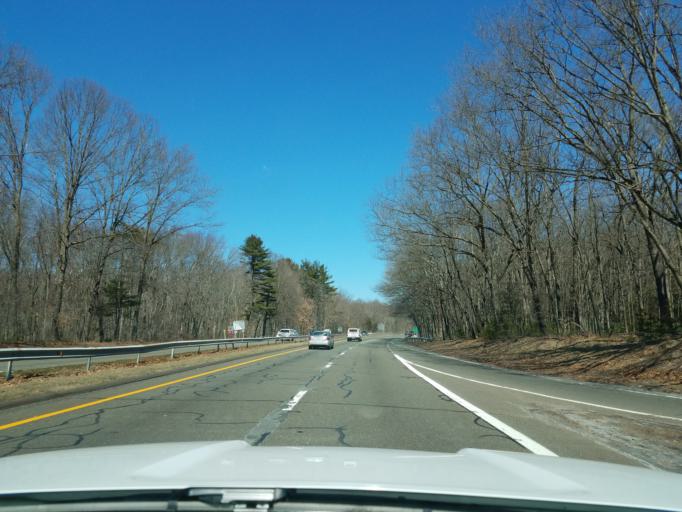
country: US
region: Connecticut
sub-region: New Haven County
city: Orange
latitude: 41.3074
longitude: -73.0332
